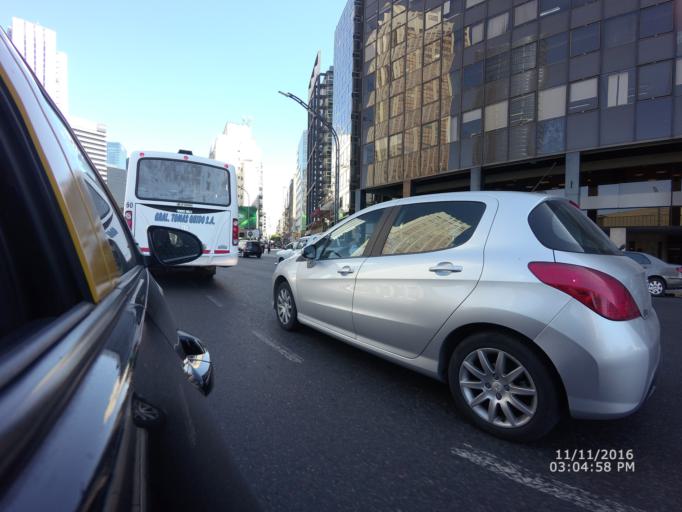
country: AR
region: Buenos Aires F.D.
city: Retiro
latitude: -34.5946
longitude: -58.3736
